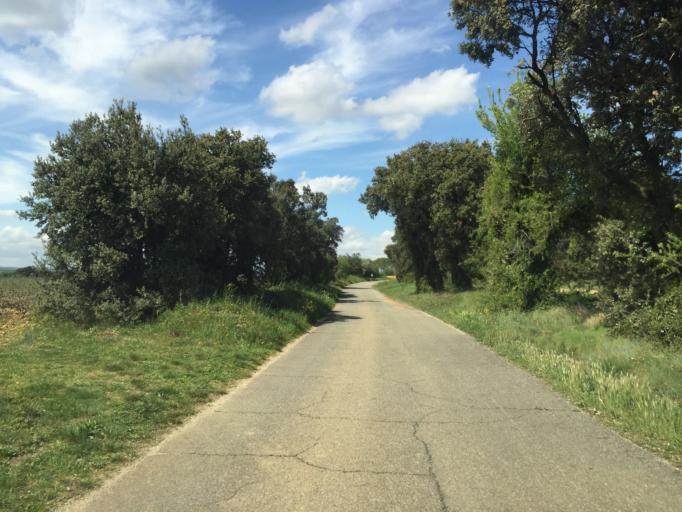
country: FR
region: Provence-Alpes-Cote d'Azur
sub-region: Departement du Vaucluse
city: Chateauneuf-du-Pape
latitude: 44.0467
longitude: 4.8397
